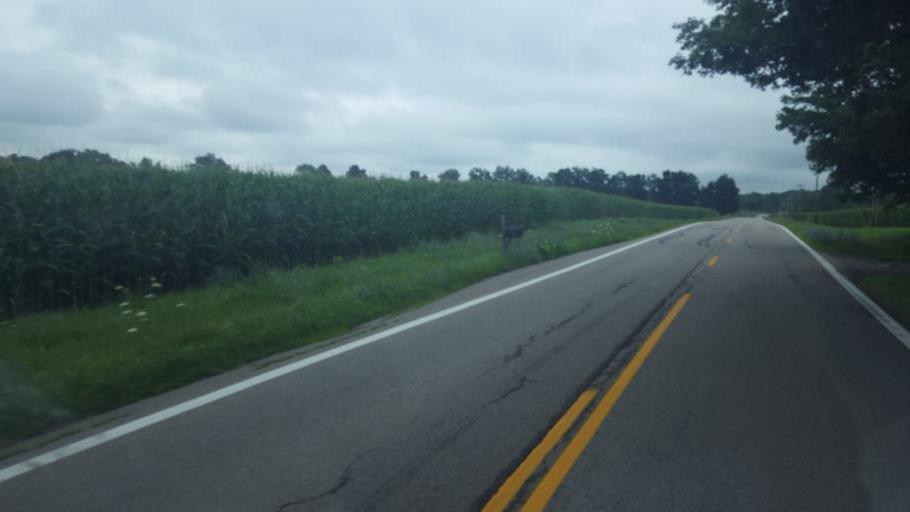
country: US
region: Ohio
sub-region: Delaware County
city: Sunbury
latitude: 40.3214
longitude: -82.8513
